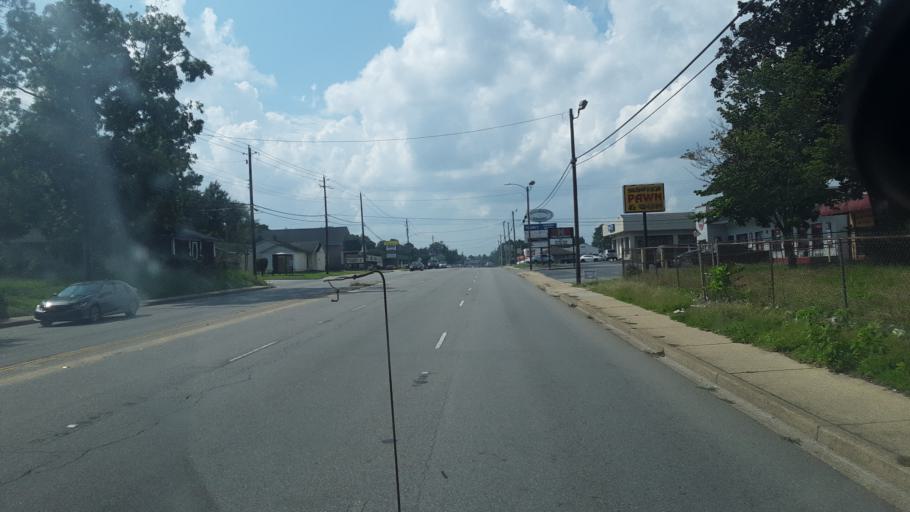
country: US
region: South Carolina
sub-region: Sumter County
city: Sumter
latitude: 33.9405
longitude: -80.3651
